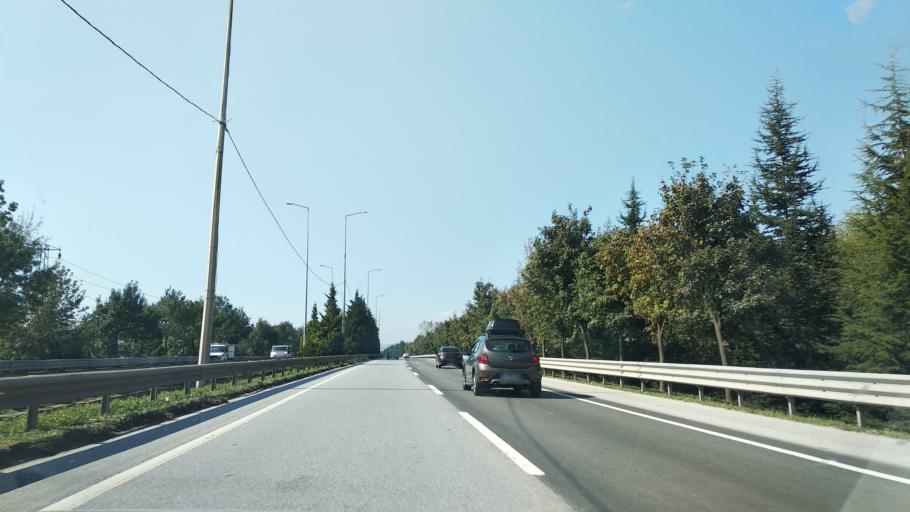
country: TR
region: Kocaeli
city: Kosekoy
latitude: 40.7550
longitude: 30.0126
